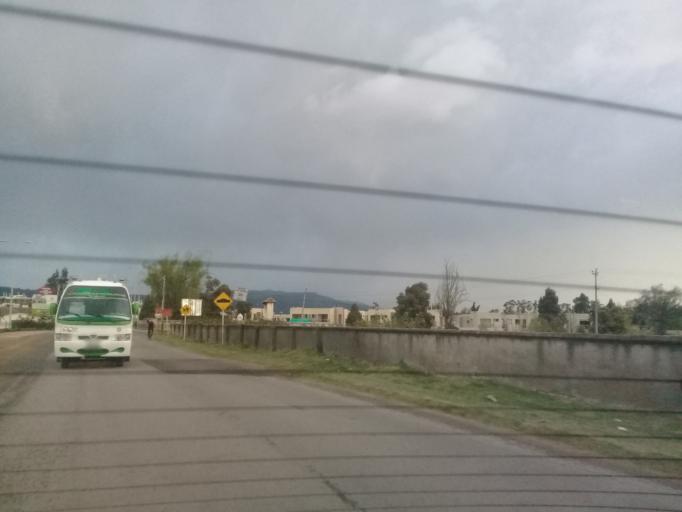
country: CO
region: Cundinamarca
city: Cajica
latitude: 4.9265
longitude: -74.0480
